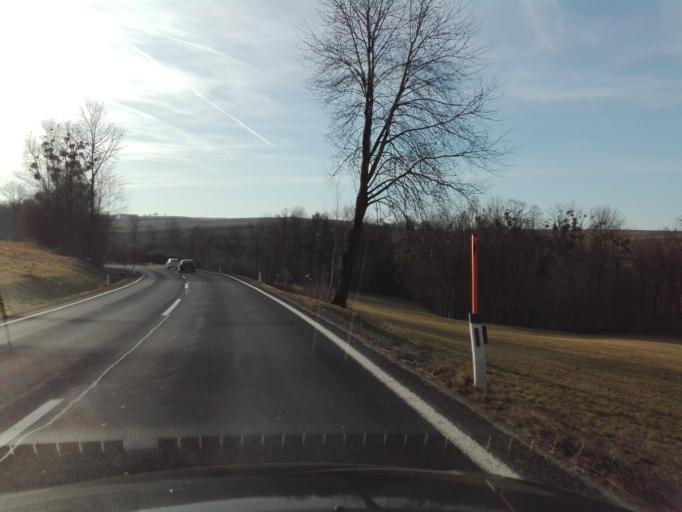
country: AT
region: Lower Austria
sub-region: Politischer Bezirk Amstetten
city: Sankt Valentin
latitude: 48.1805
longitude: 14.5824
